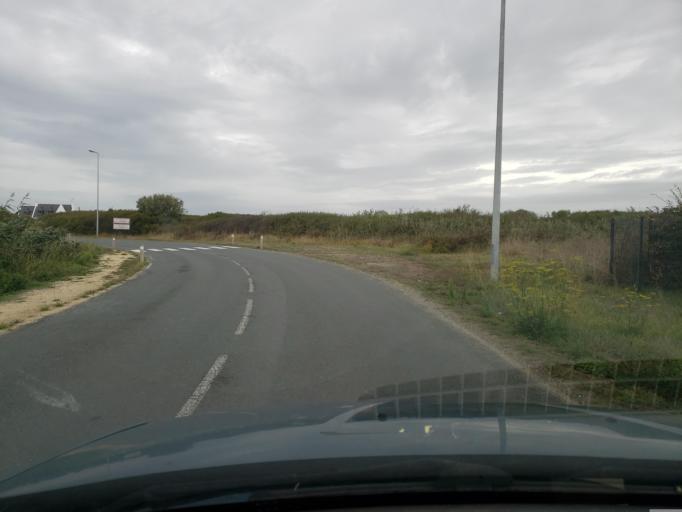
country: FR
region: Brittany
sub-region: Departement du Finistere
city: Plomeur
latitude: 47.8142
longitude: -4.3607
